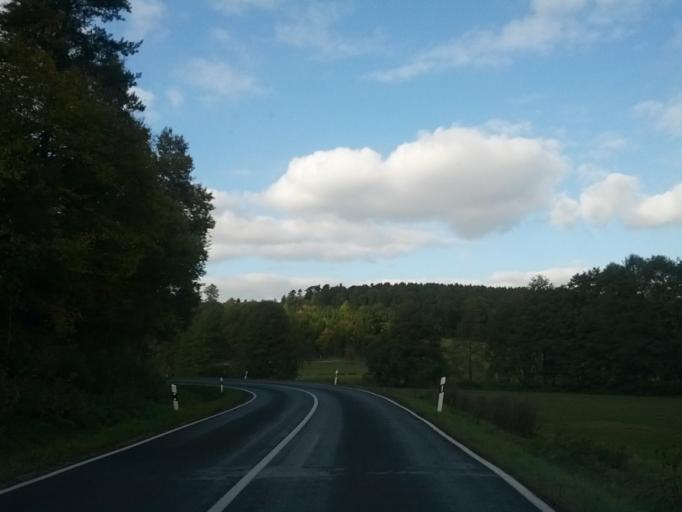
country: DE
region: Thuringia
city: Marksuhl
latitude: 50.9369
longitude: 10.1532
